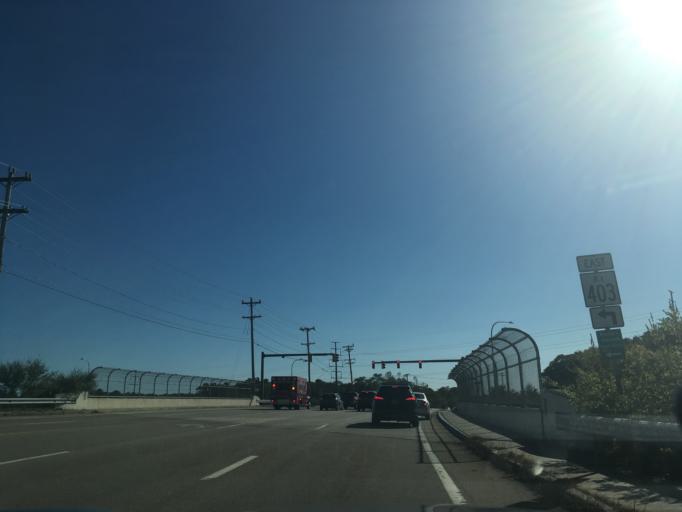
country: US
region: Rhode Island
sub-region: Washington County
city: North Kingstown
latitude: 41.6041
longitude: -71.4548
